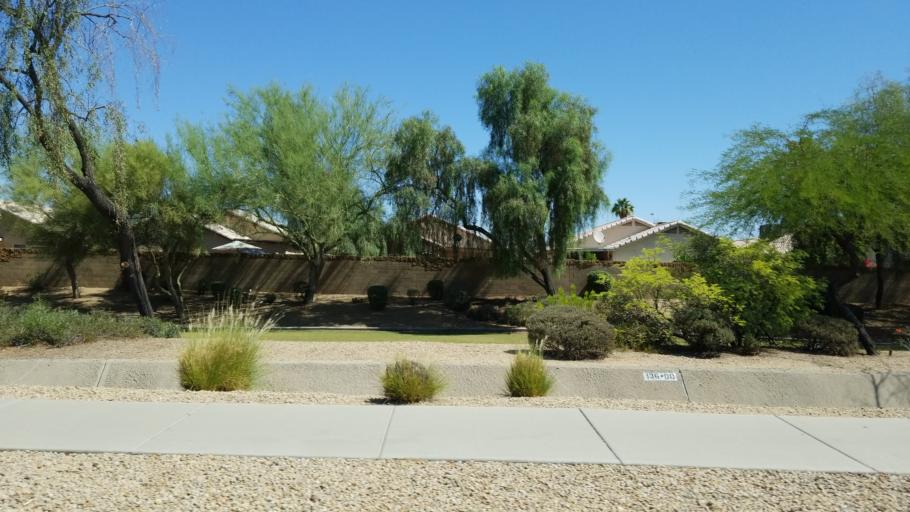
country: US
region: Arizona
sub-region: Maricopa County
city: Tolleson
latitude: 33.4935
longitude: -112.2952
